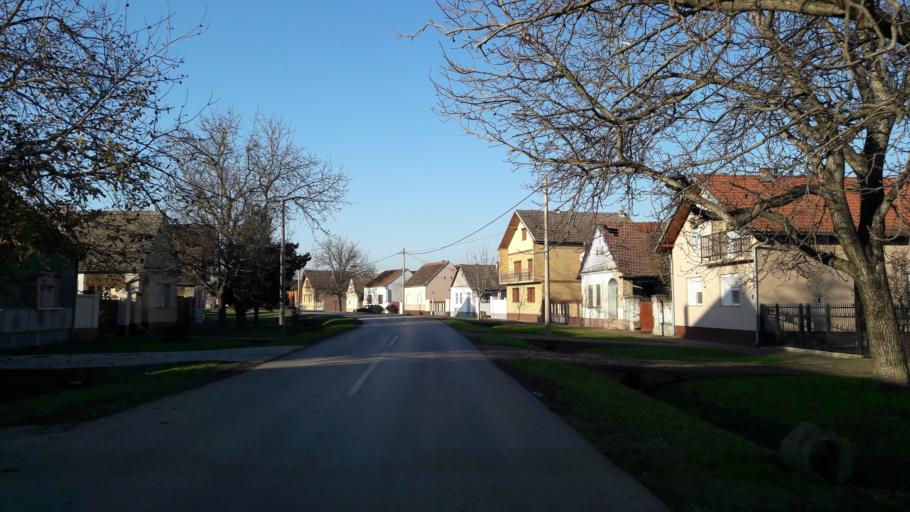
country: HR
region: Osjecko-Baranjska
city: Semeljci
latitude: 45.3885
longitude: 18.5609
